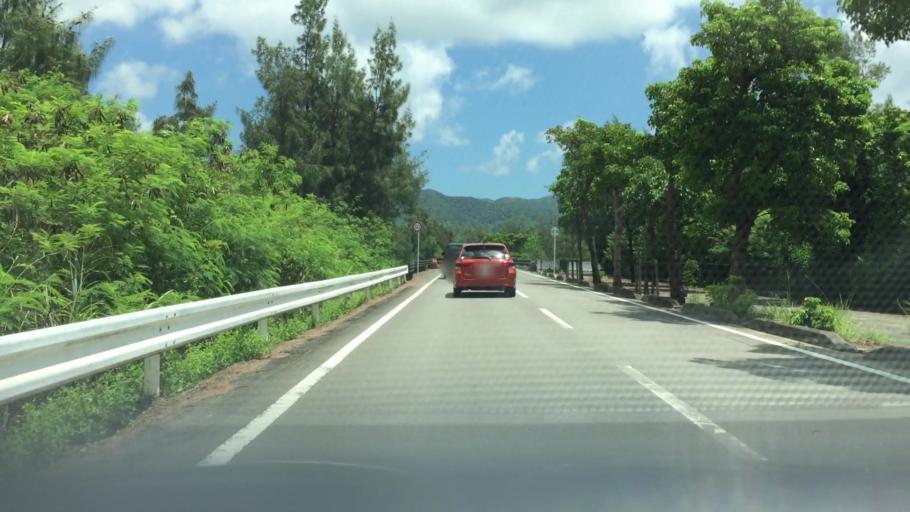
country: JP
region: Okinawa
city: Ishigaki
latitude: 24.3912
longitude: 124.1412
